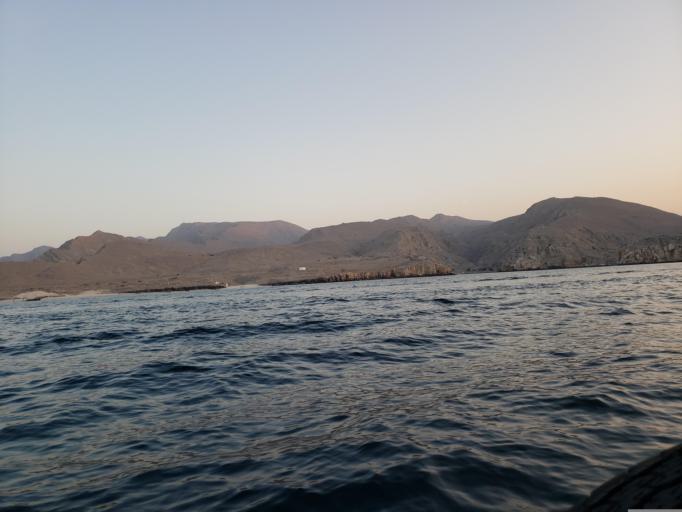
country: OM
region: Musandam
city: Dib Dibba
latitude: 26.2197
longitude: 56.2770
